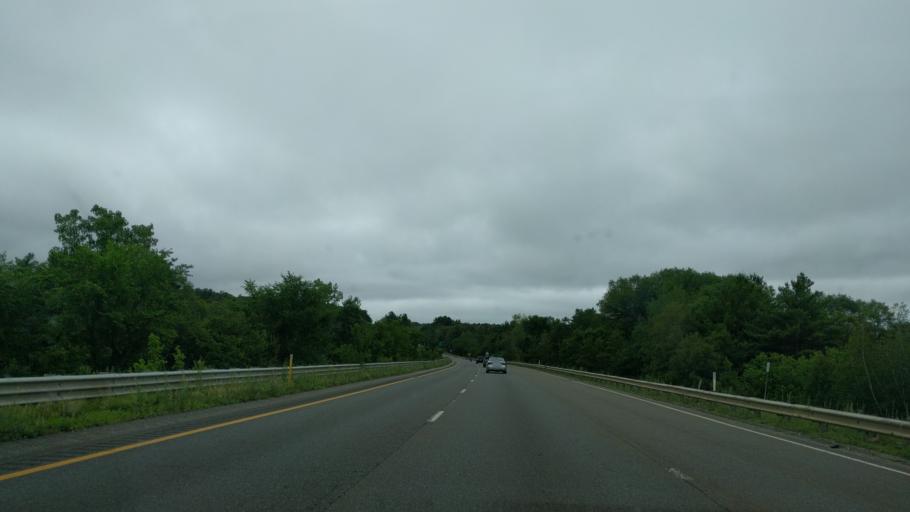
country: US
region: Massachusetts
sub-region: Worcester County
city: East Douglas
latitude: 42.0856
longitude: -71.6926
